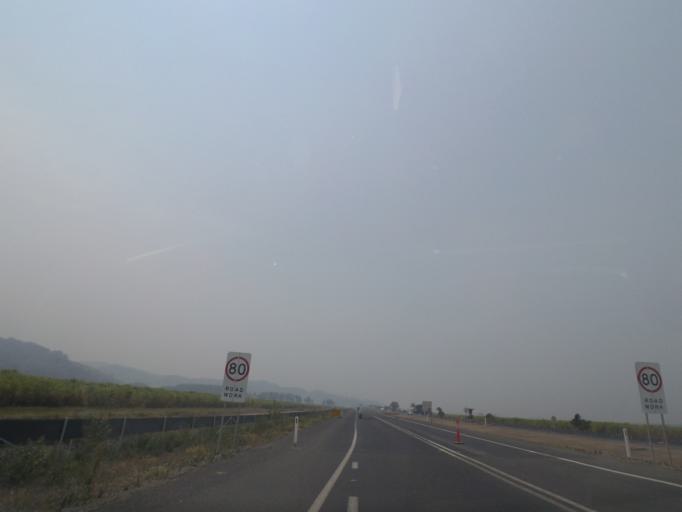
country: AU
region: New South Wales
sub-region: Ballina
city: Ballina
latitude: -28.8992
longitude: 153.4803
